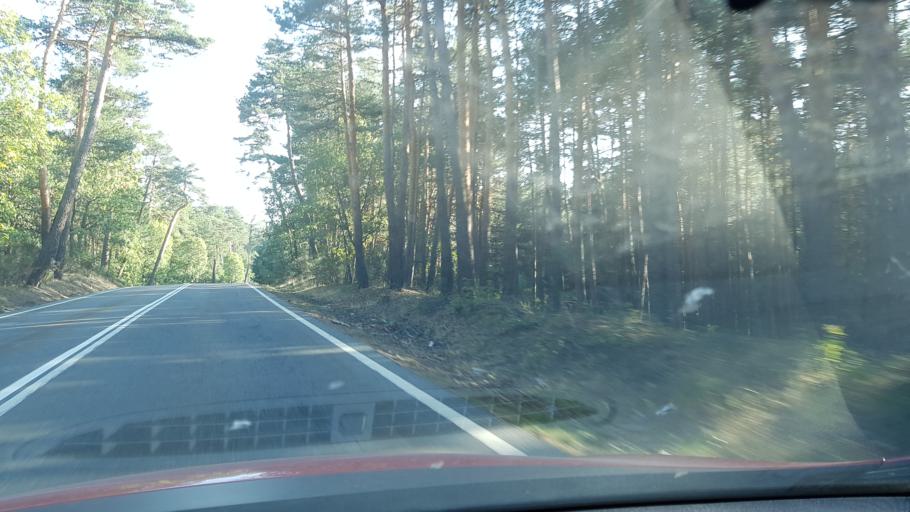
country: ES
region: Castille and Leon
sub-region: Provincia de Segovia
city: San Ildefonso
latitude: 40.8488
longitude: -4.0259
